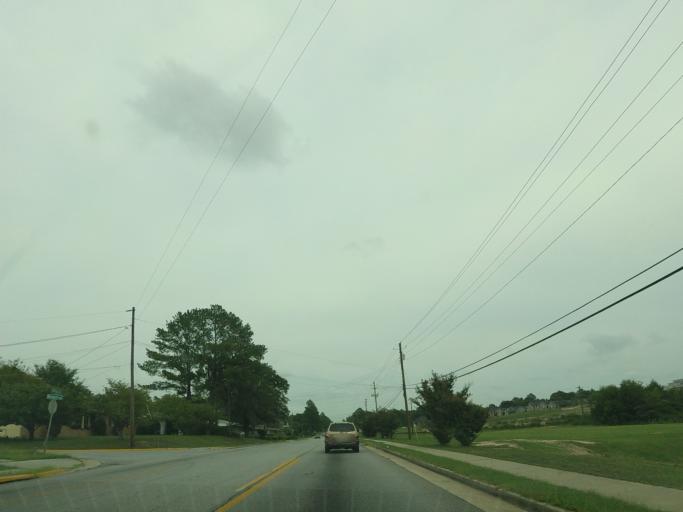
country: US
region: Georgia
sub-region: Bibb County
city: Macon
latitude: 32.8202
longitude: -83.6732
